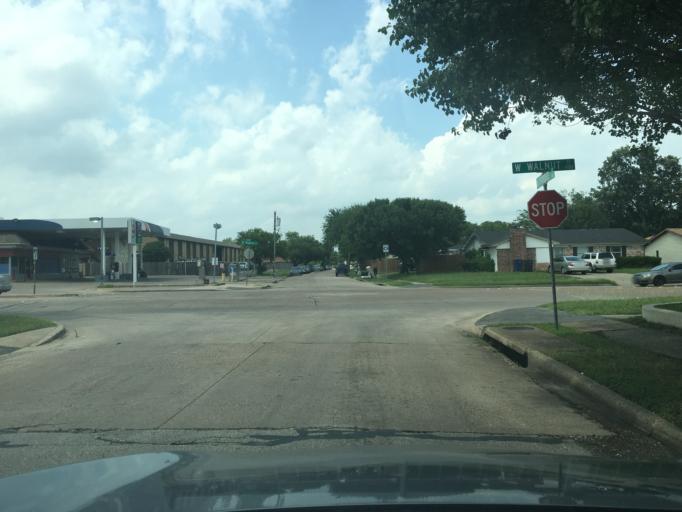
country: US
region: Texas
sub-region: Dallas County
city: Richardson
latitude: 32.9165
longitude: -96.6959
